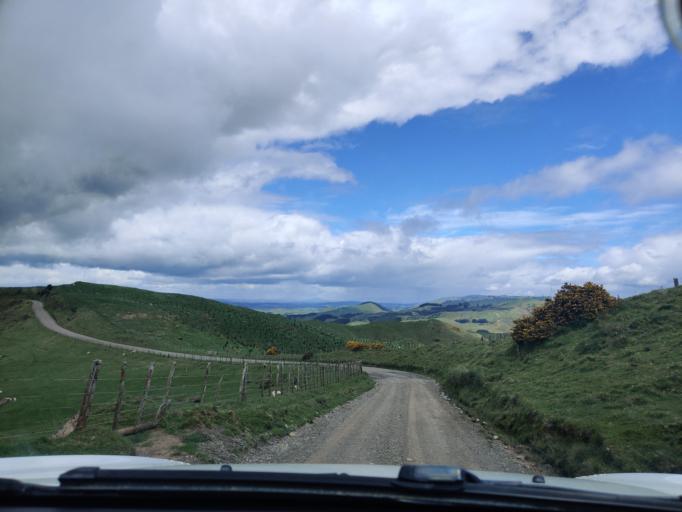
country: NZ
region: Manawatu-Wanganui
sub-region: Palmerston North City
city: Palmerston North
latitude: -40.2803
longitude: 175.8568
